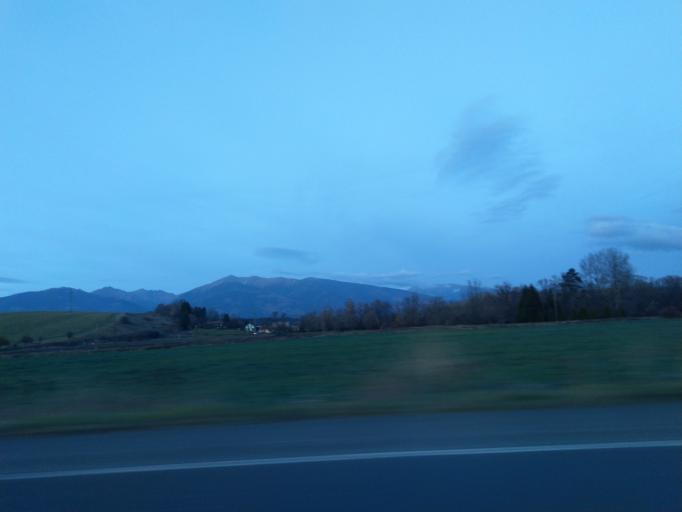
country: SK
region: Zilinsky
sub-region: Okres Liptovsky Mikulas
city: Liptovsky Mikulas
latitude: 49.0693
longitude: 19.6753
